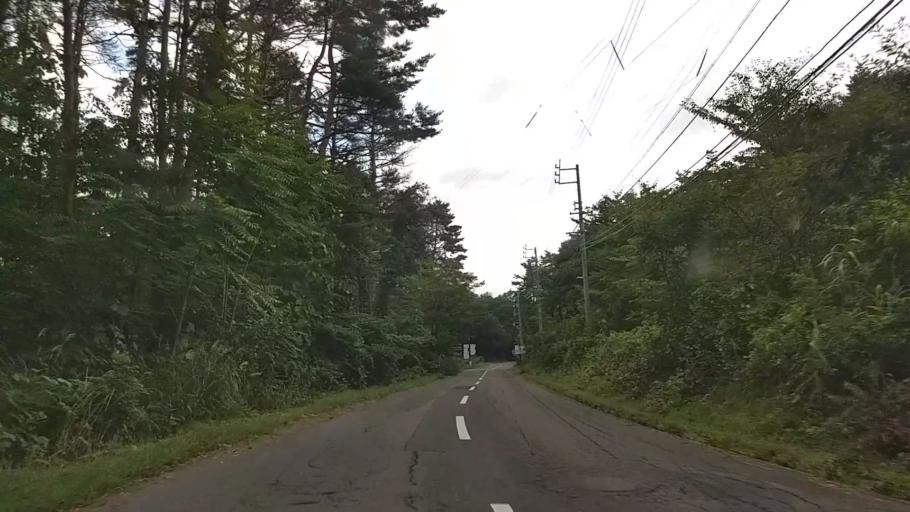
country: JP
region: Nagano
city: Iiyama
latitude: 36.8208
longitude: 138.3985
